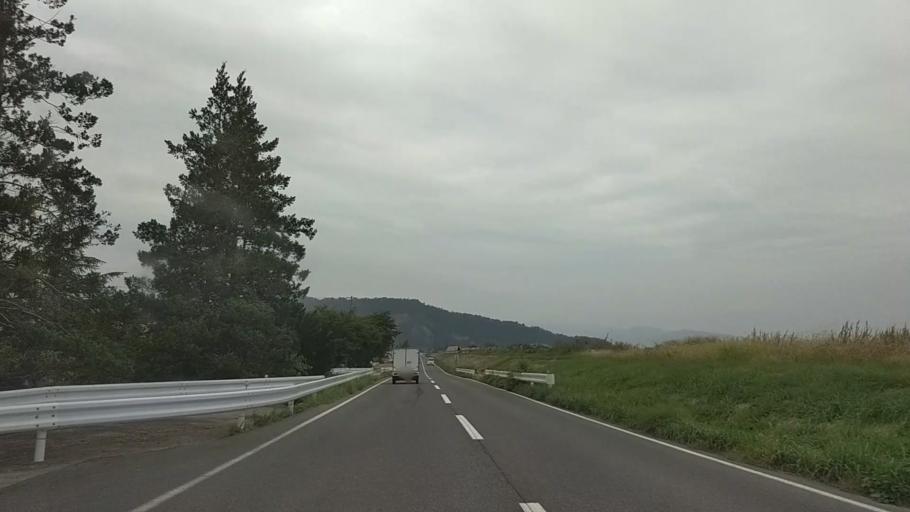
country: JP
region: Nagano
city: Nagano-shi
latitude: 36.5981
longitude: 138.2187
